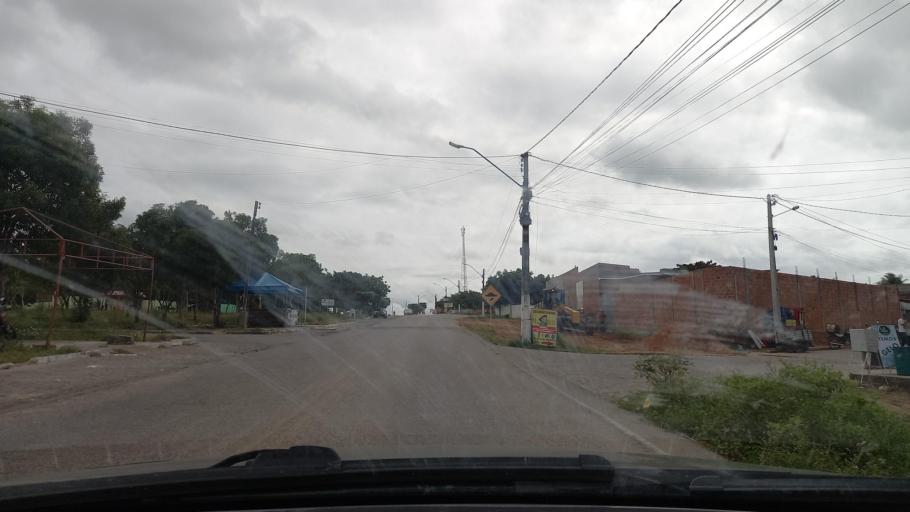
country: BR
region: Sergipe
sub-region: Caninde De Sao Francisco
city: Caninde de Sao Francisco
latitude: -9.6130
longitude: -37.7619
